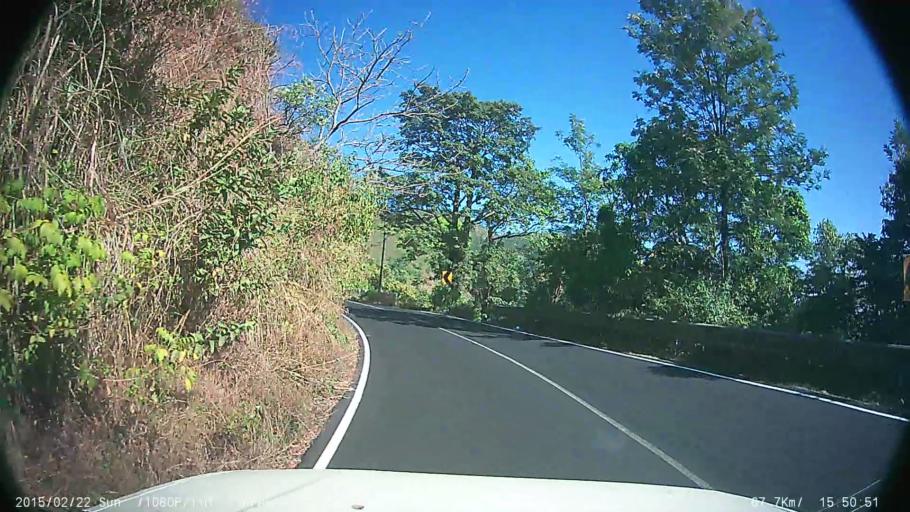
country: IN
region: Kerala
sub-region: Kottayam
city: Erattupetta
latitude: 9.5689
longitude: 77.0052
